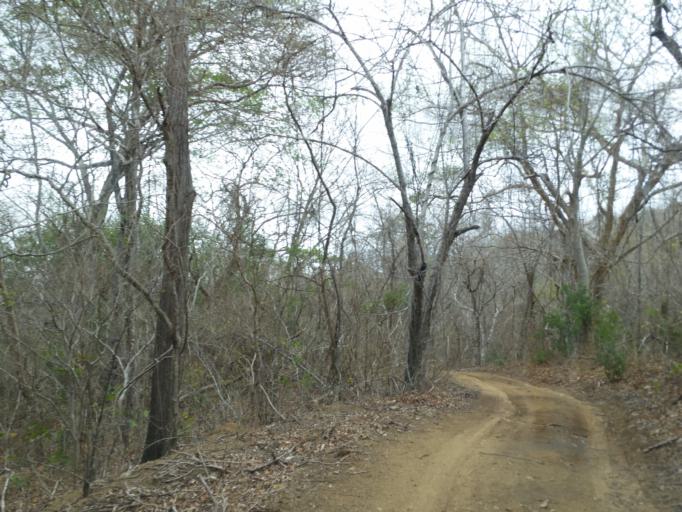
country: NI
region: Rivas
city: Tola
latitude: 11.4265
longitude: -86.0710
